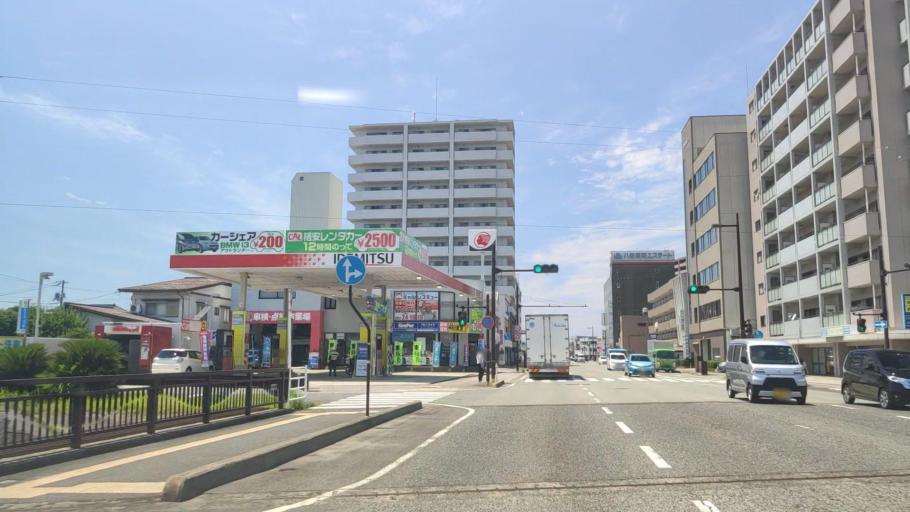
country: JP
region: Tottori
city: Tottori
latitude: 35.4903
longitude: 134.2263
